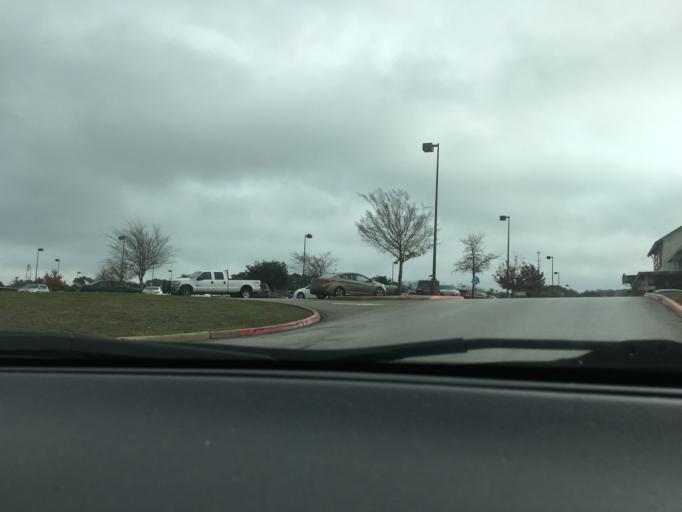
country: US
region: Texas
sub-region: Hays County
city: Dripping Springs
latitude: 30.1899
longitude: -98.0826
